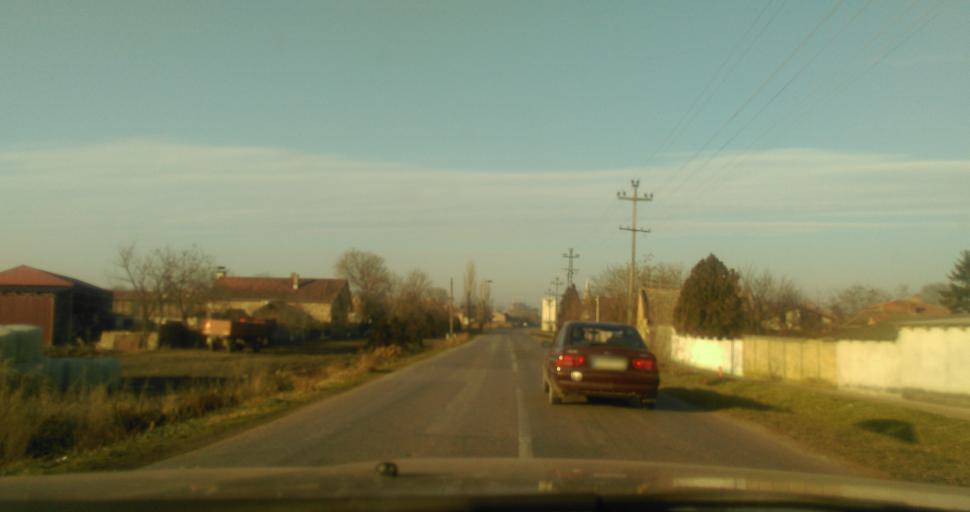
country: RS
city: Backo Gradiste
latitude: 45.5270
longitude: 20.0245
